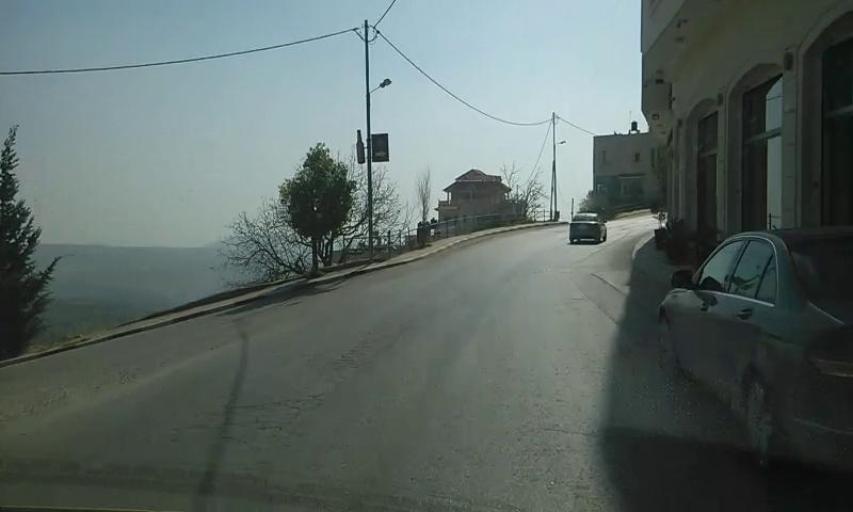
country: PS
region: West Bank
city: At Taybah
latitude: 31.9554
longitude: 35.2997
